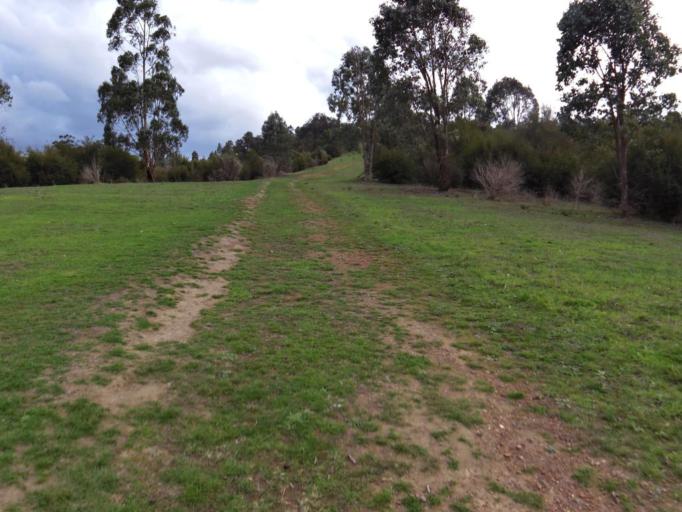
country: AU
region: Victoria
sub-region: Yarra Ranges
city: Chirnside Park
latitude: -37.7100
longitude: 145.2917
